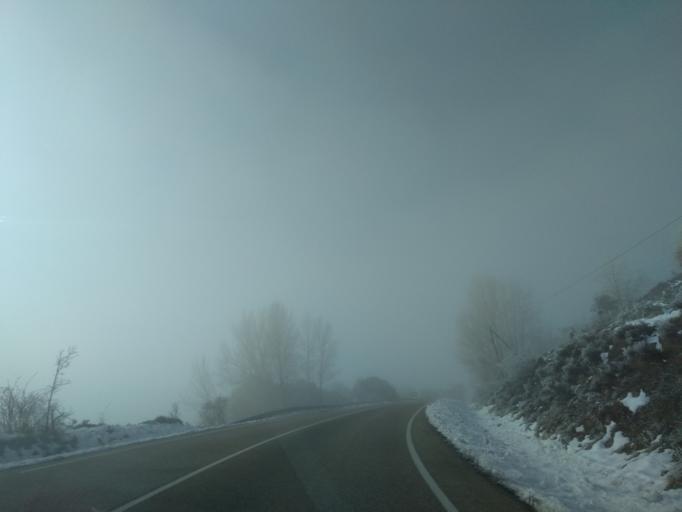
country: ES
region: Castille and Leon
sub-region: Provincia de Burgos
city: Medina de Pomar
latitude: 42.9978
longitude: -3.5181
